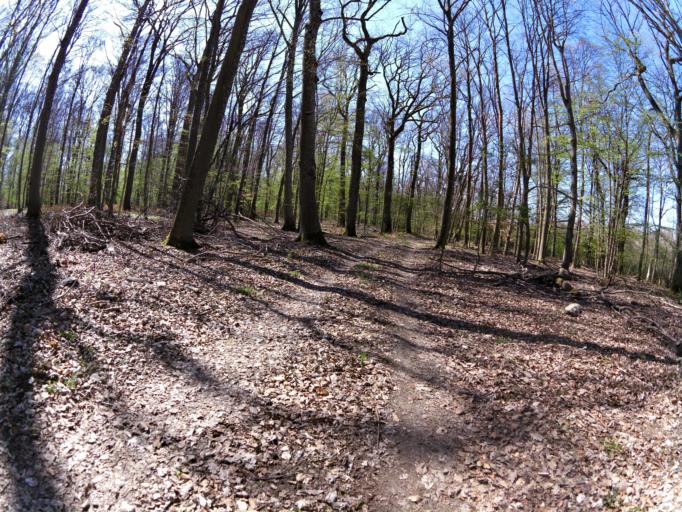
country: DE
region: Bavaria
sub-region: Regierungsbezirk Unterfranken
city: Hettstadt
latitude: 49.8198
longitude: 9.8064
